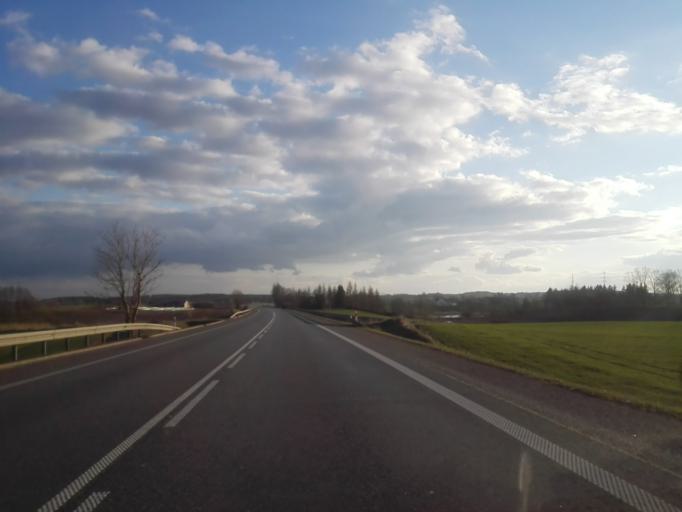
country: PL
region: Podlasie
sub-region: Suwalki
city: Suwalki
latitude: 54.1839
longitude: 23.0019
